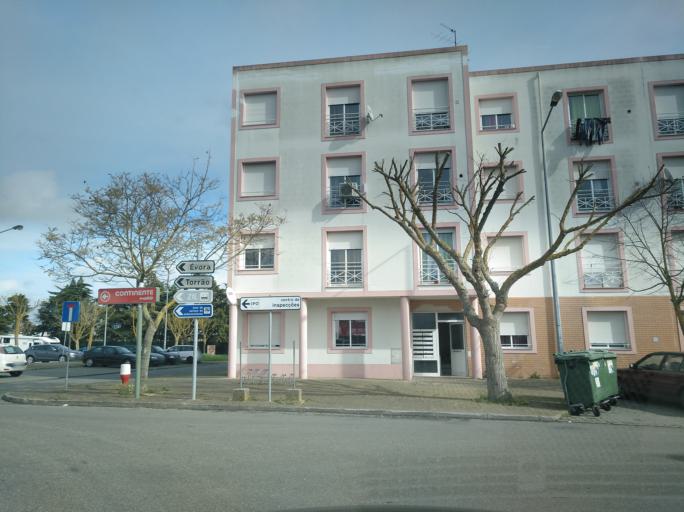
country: PT
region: Setubal
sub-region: Grandola
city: Grandola
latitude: 38.1836
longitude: -8.5649
